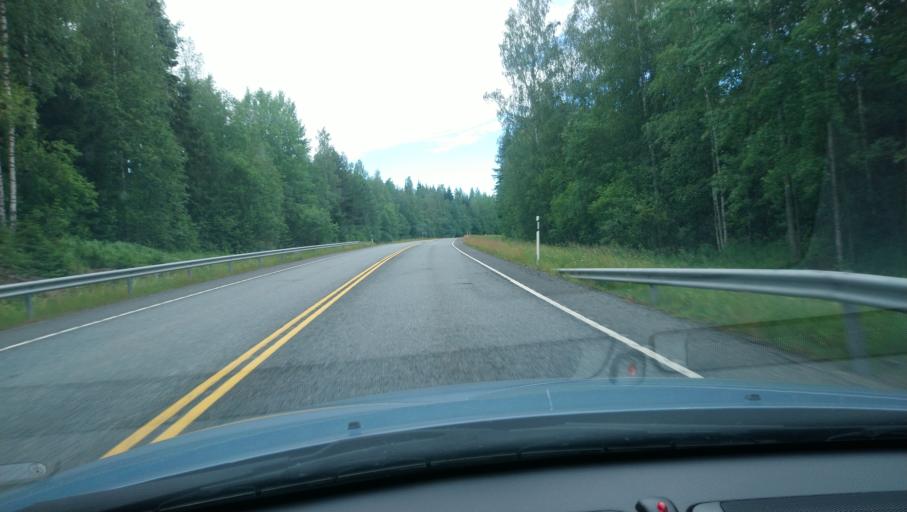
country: FI
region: Uusimaa
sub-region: Porvoo
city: Porvoo
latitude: 60.4343
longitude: 25.5747
